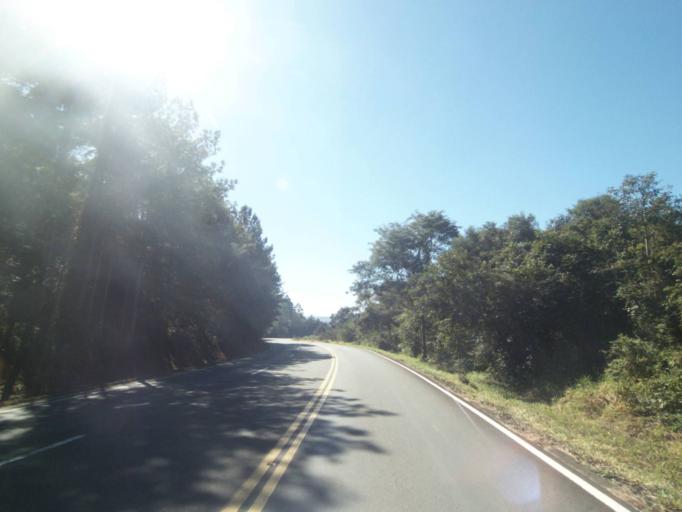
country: BR
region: Parana
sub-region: Tibagi
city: Tibagi
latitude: -24.4755
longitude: -50.5090
